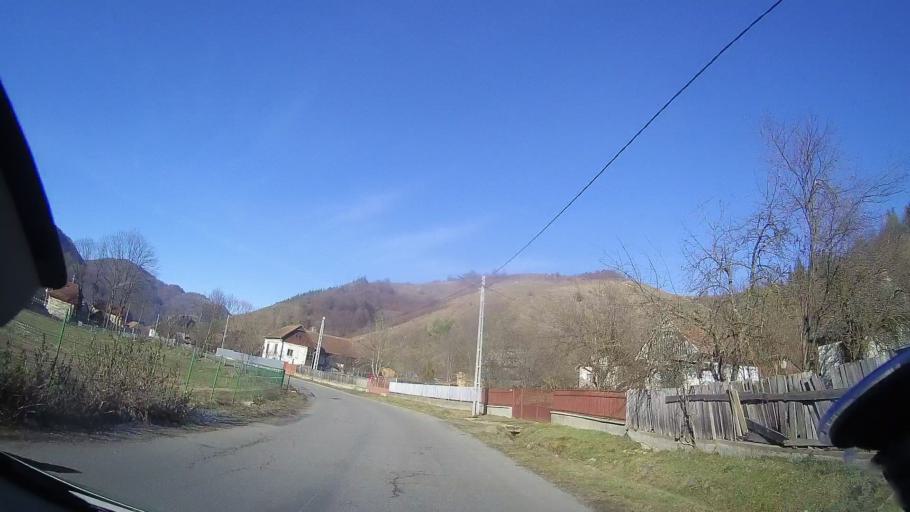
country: RO
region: Cluj
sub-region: Comuna Sacueu
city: Sacuieu
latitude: 46.8273
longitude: 22.8825
